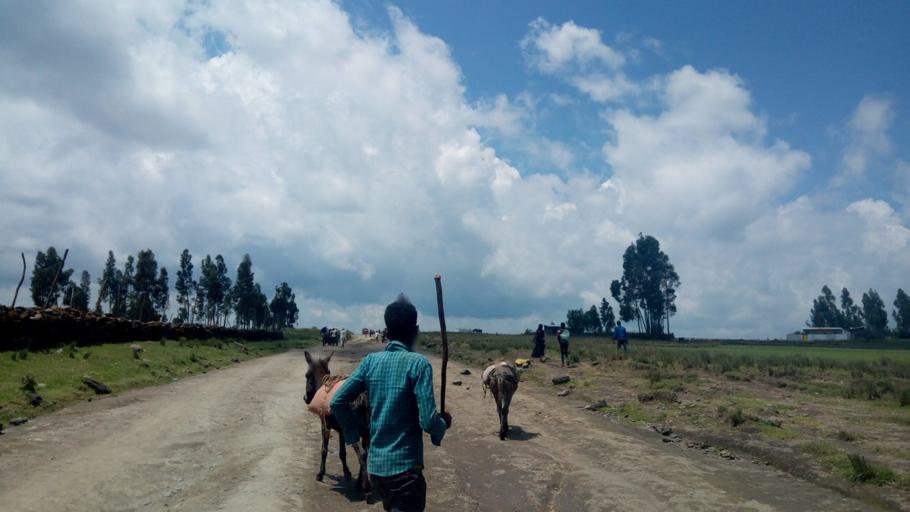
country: ET
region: Oromiya
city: Sendafa
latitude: 8.9825
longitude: 39.1251
